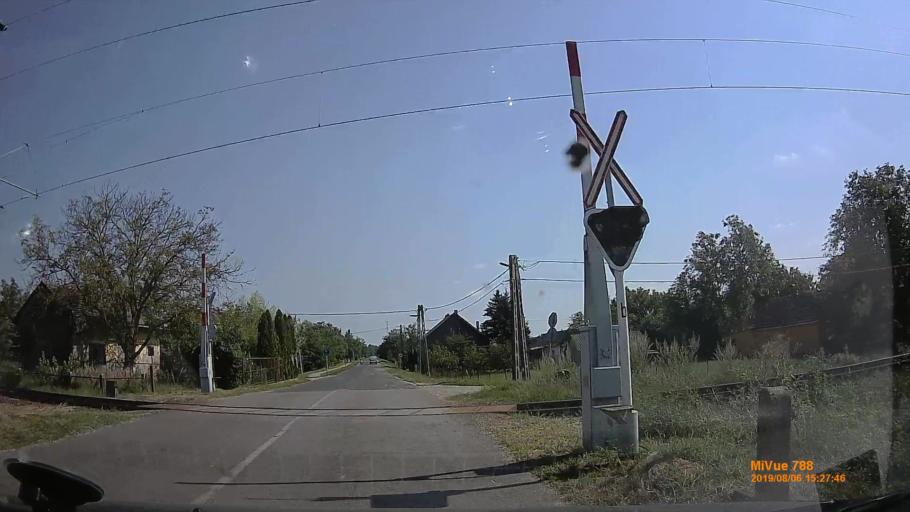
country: HR
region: Koprivnicko-Krizevacka
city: Drnje
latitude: 46.2503
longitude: 16.9709
